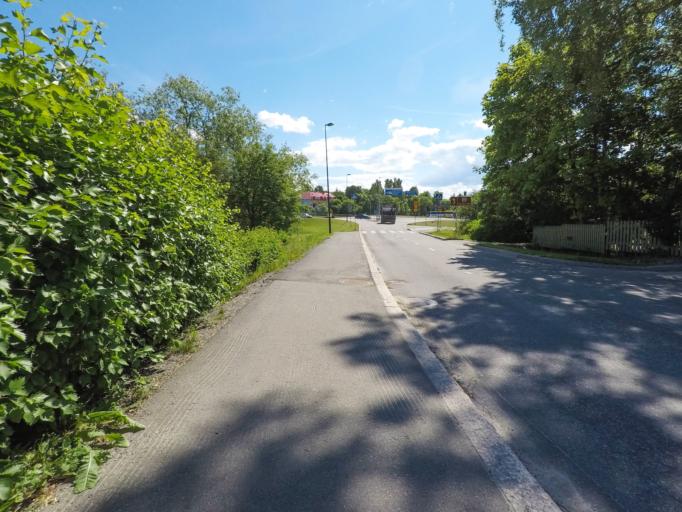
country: FI
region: Southern Savonia
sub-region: Savonlinna
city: Savonlinna
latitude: 61.8696
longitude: 28.8999
